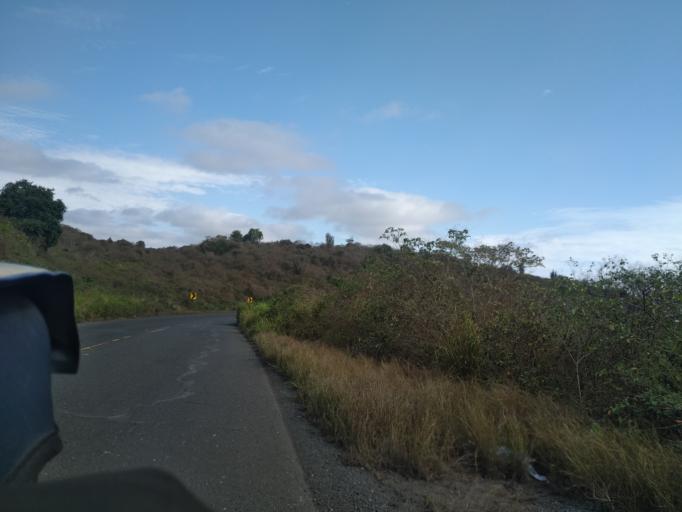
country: EC
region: Manabi
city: Jipijapa
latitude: -1.4445
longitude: -80.7557
